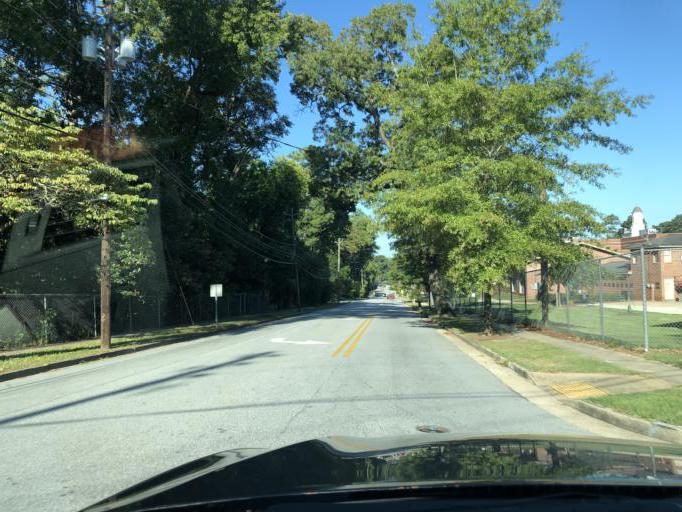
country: US
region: Georgia
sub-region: Muscogee County
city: Columbus
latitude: 32.4786
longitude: -84.9612
